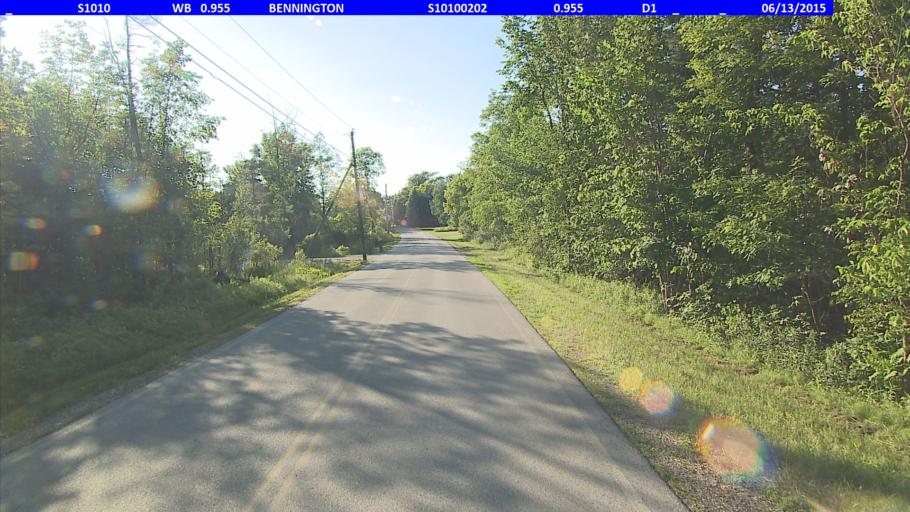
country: US
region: Vermont
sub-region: Bennington County
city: Bennington
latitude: 42.8754
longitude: -73.1581
